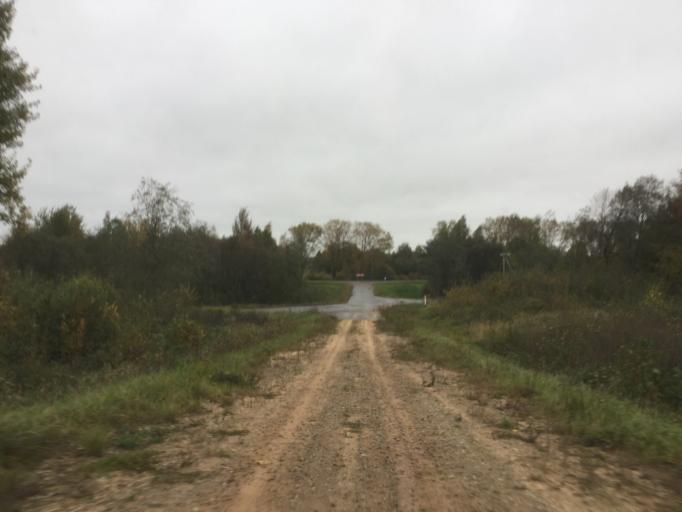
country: BY
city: Novolukoml'
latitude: 54.7333
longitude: 29.1405
